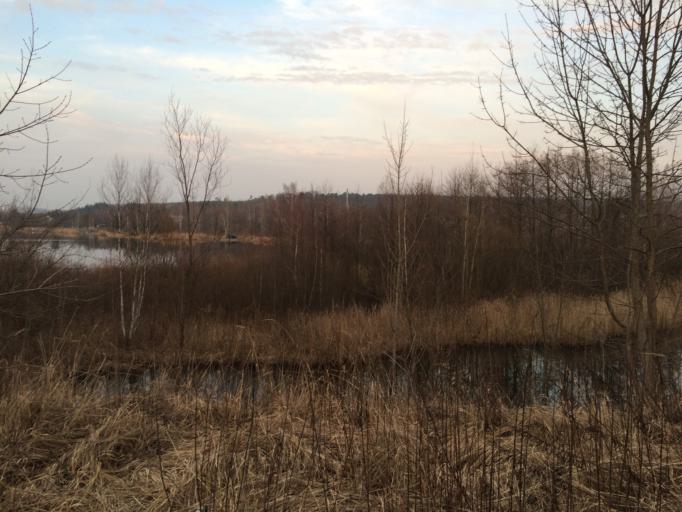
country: PL
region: Swietokrzyskie
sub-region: Powiat starachowicki
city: Starachowice
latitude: 51.0178
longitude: 21.0783
